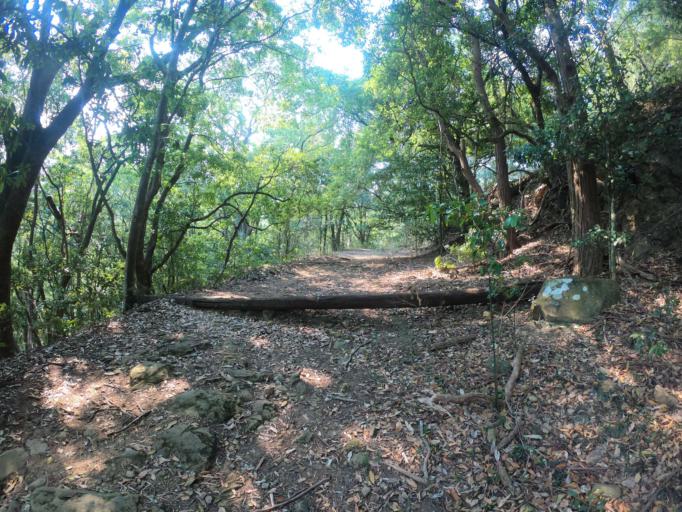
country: AU
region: New South Wales
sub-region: Wollongong
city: Bulli
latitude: -34.3260
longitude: 150.8884
